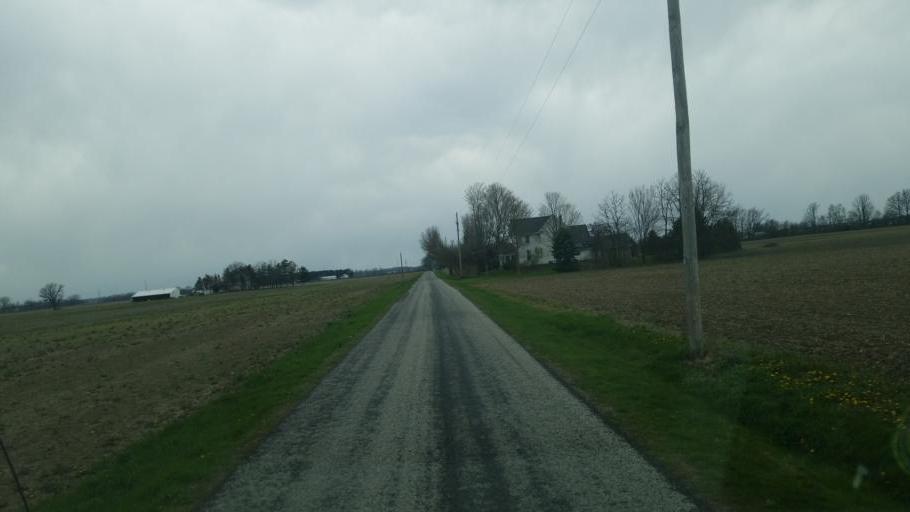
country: US
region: Ohio
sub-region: Marion County
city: Prospect
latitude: 40.4047
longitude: -83.1331
